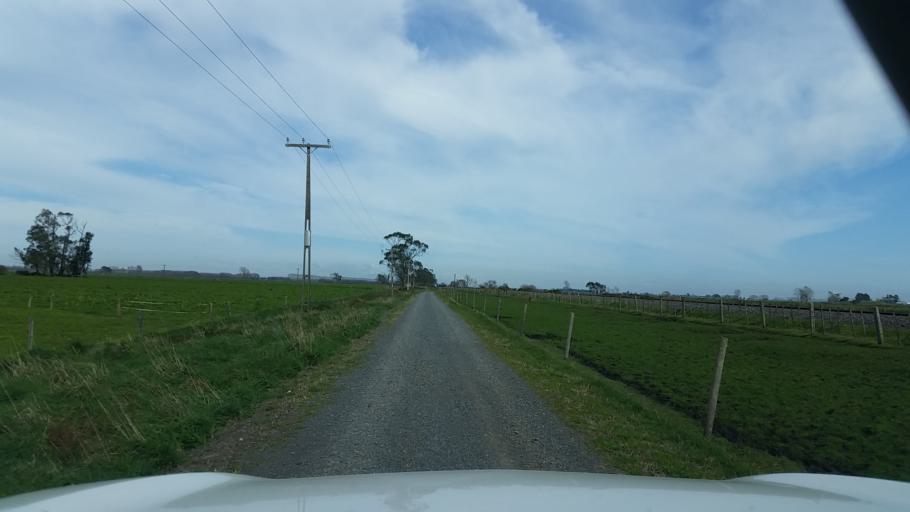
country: NZ
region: Waikato
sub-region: Waipa District
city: Cambridge
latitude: -37.6831
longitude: 175.4546
